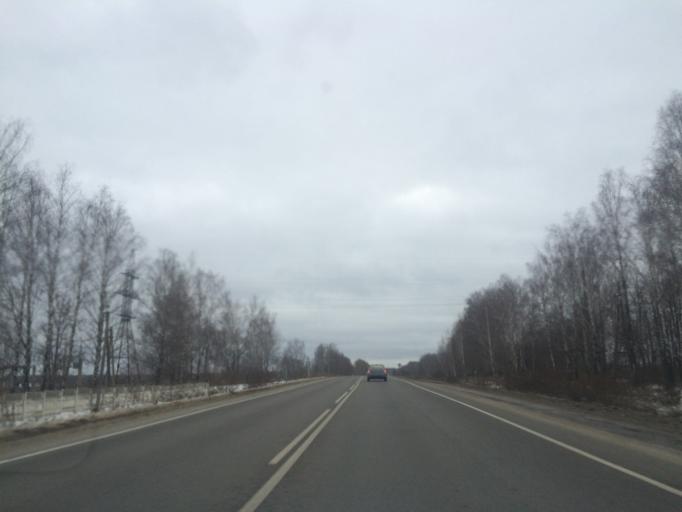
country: RU
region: Tula
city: Barsuki
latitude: 54.1455
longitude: 37.3945
